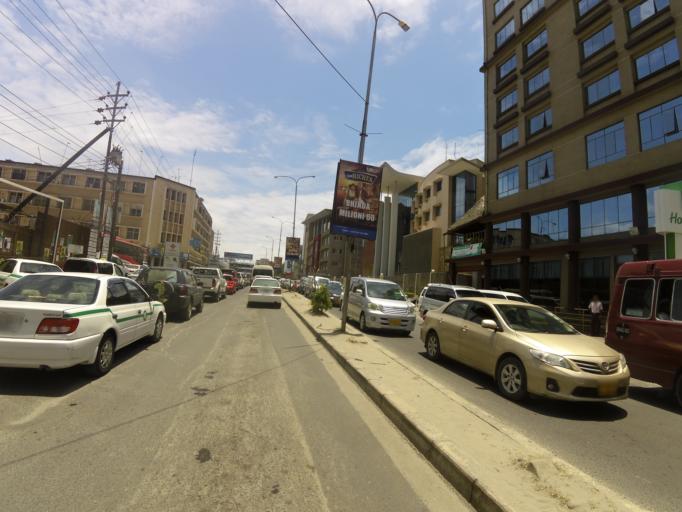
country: TZ
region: Dar es Salaam
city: Dar es Salaam
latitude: -6.8134
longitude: 39.2865
